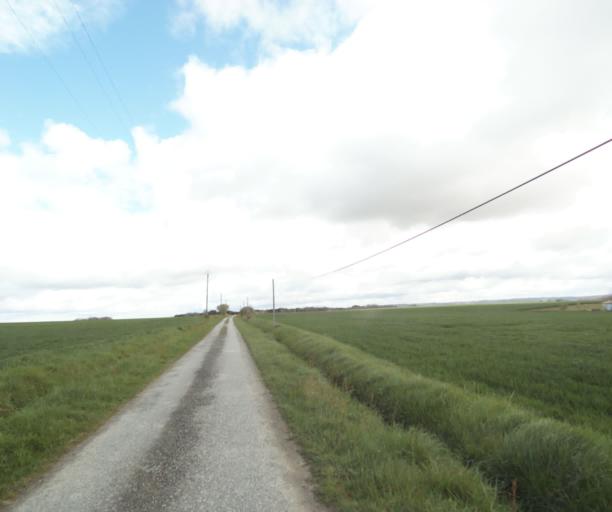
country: FR
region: Midi-Pyrenees
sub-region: Departement de l'Ariege
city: Saverdun
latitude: 43.2315
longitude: 1.5486
